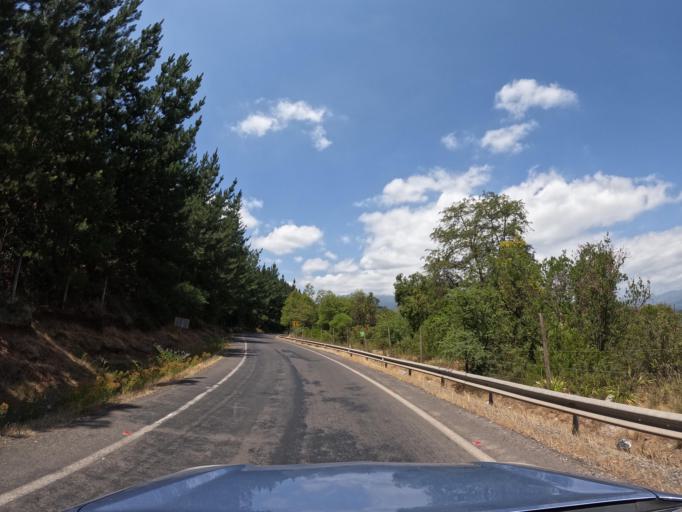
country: CL
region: Maule
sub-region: Provincia de Curico
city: Molina
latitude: -35.1764
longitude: -71.1031
